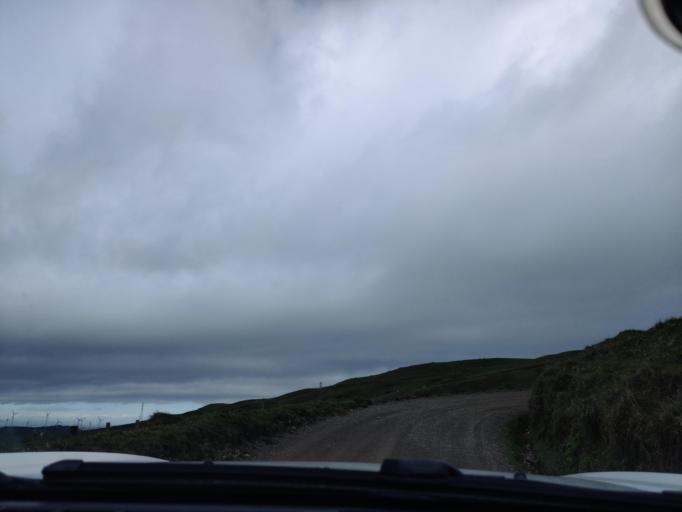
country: NZ
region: Manawatu-Wanganui
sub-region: Palmerston North City
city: Palmerston North
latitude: -40.2748
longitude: 175.8497
